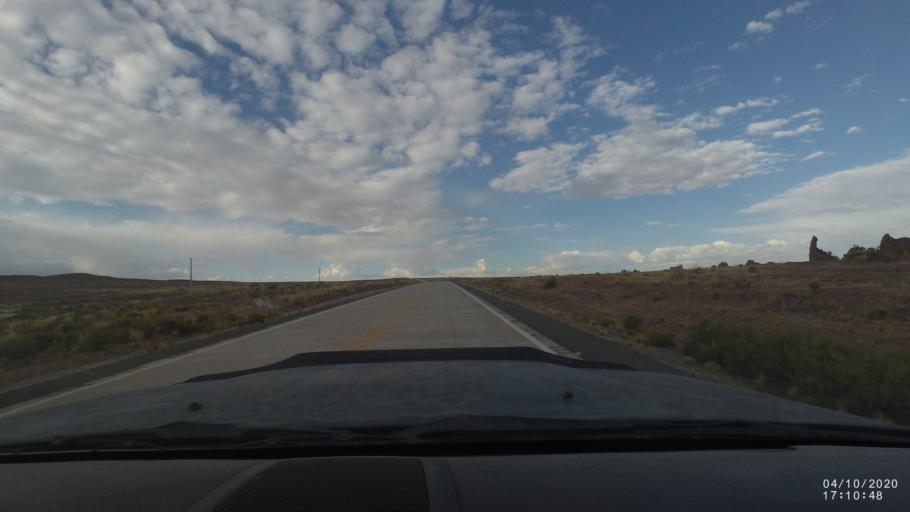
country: BO
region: Oruro
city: Oruro
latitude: -18.3270
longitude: -67.5810
